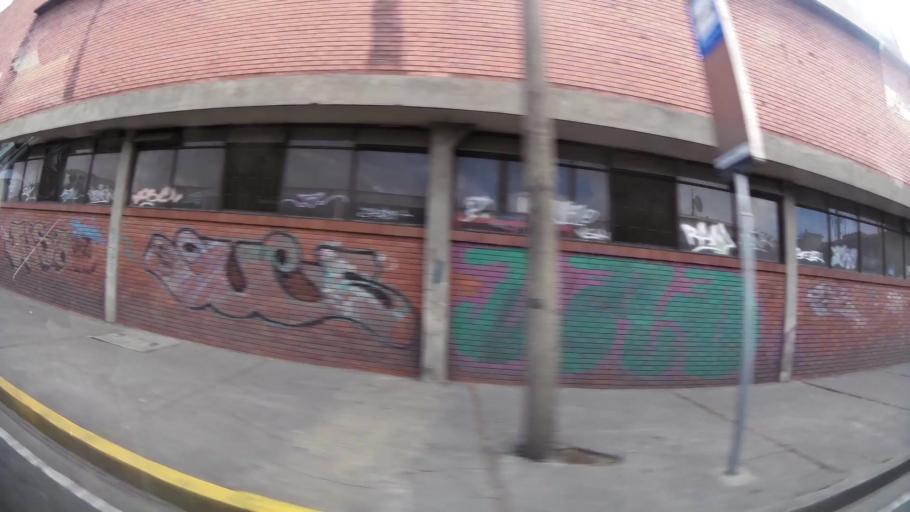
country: CO
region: Bogota D.C.
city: Bogota
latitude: 4.6219
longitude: -74.0918
